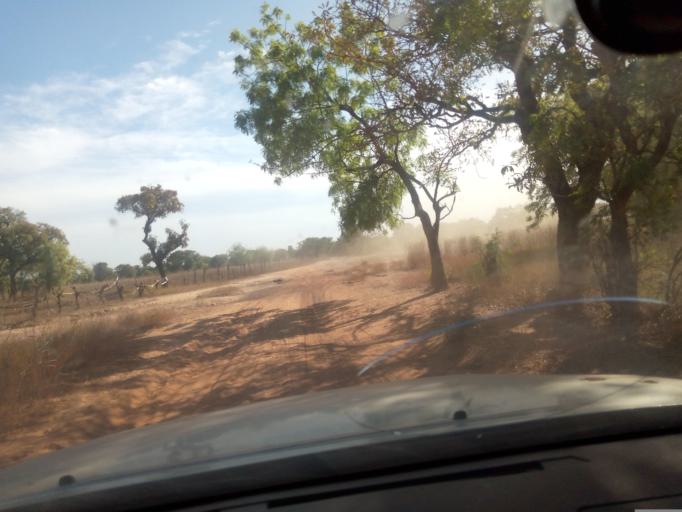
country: ML
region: Sikasso
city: Sikasso
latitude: 11.4773
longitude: -5.3313
